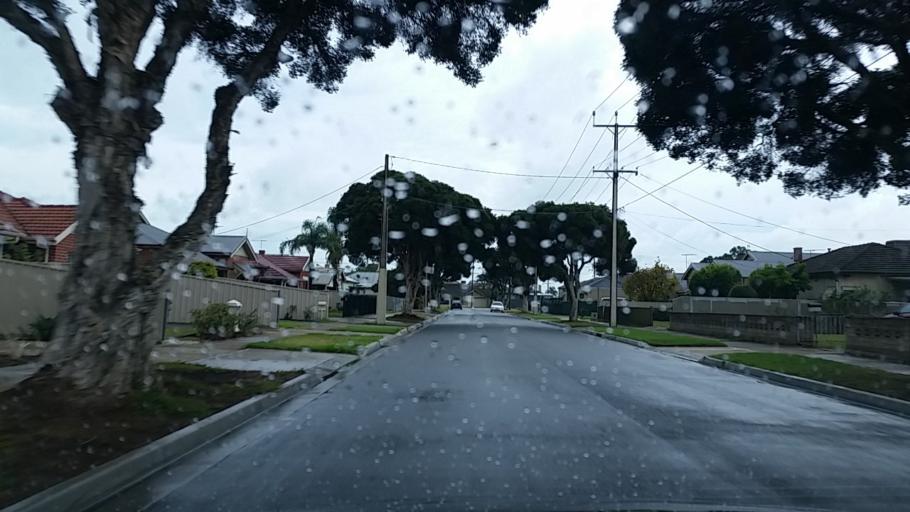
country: AU
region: South Australia
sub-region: Charles Sturt
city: Seaton
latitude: -34.8948
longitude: 138.5189
